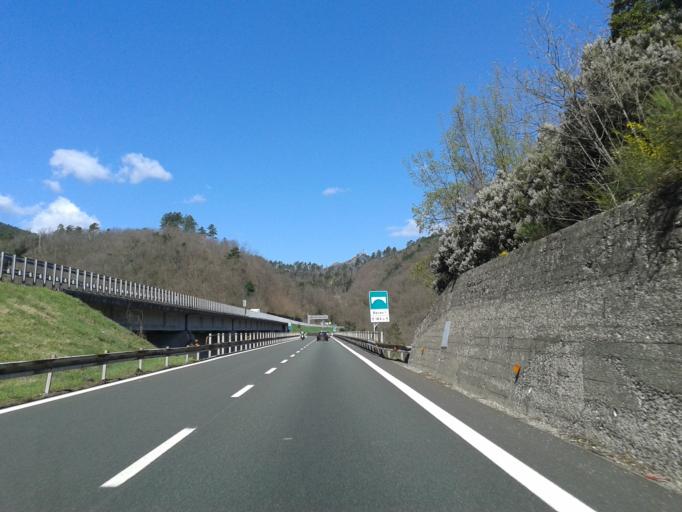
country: IT
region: Liguria
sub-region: Provincia di La Spezia
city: Carrodano
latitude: 44.2300
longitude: 9.6079
